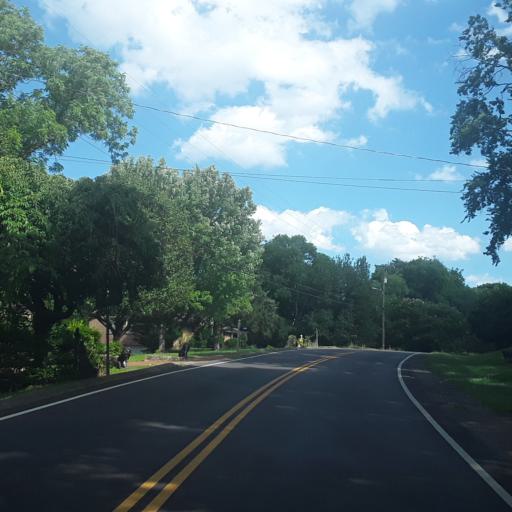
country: US
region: Tennessee
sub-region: Davidson County
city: Lakewood
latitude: 36.1924
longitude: -86.6313
